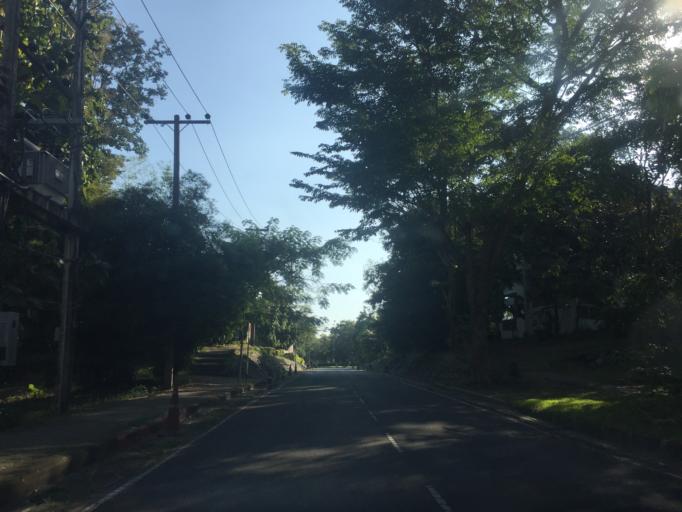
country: TH
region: Chiang Mai
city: Chiang Mai
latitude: 18.8039
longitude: 98.9522
